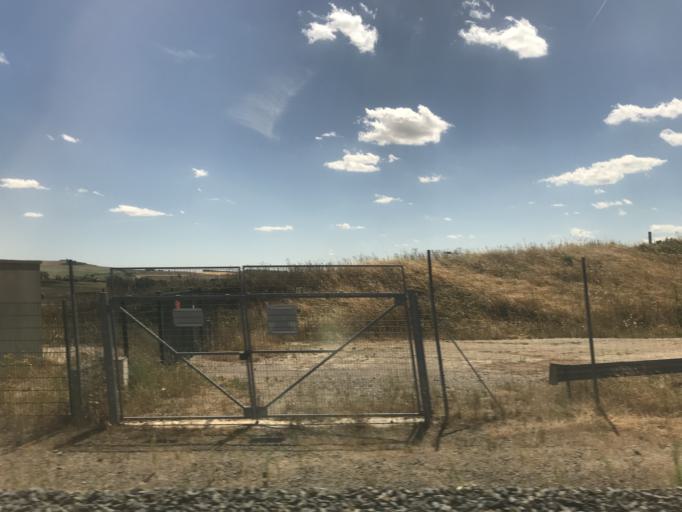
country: FR
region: Lorraine
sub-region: Departement de la Moselle
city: Solgne
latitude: 48.9588
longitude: 6.3074
